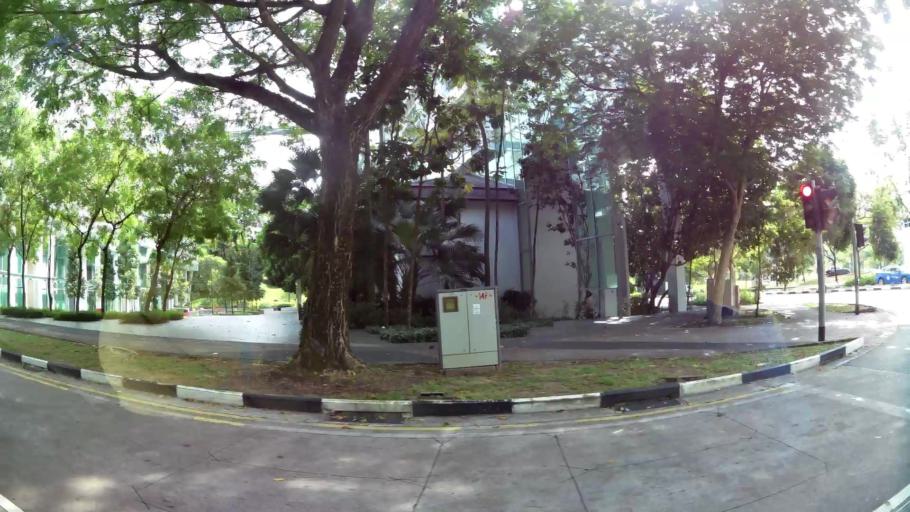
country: SG
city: Singapore
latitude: 1.3016
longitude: 103.7896
